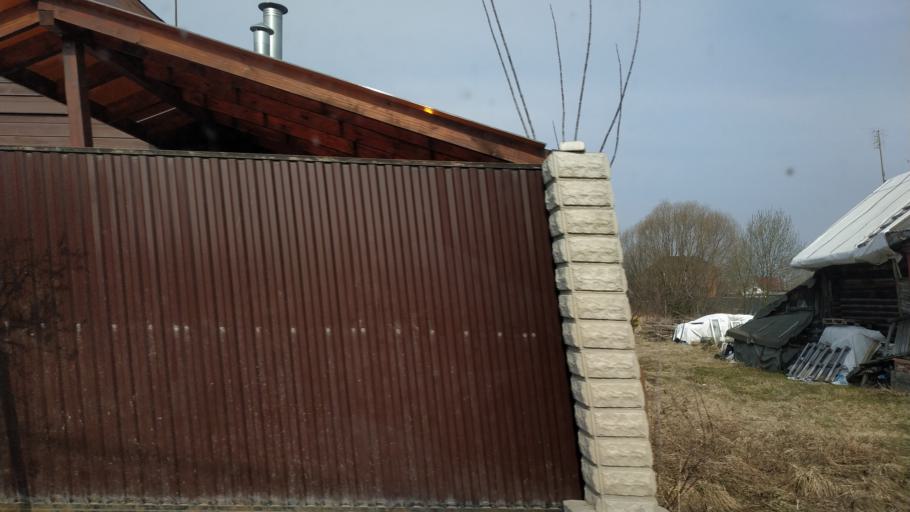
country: RU
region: Moskovskaya
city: Beloozerskiy
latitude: 55.4388
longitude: 38.4888
